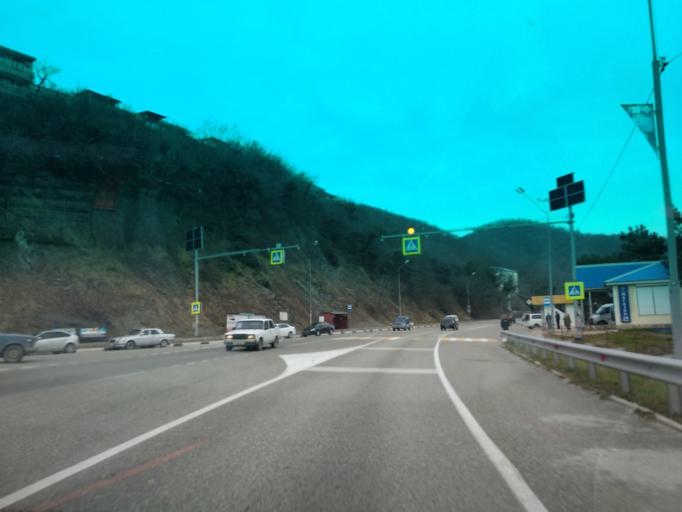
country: RU
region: Krasnodarskiy
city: Ol'ginka
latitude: 44.1995
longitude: 38.8882
